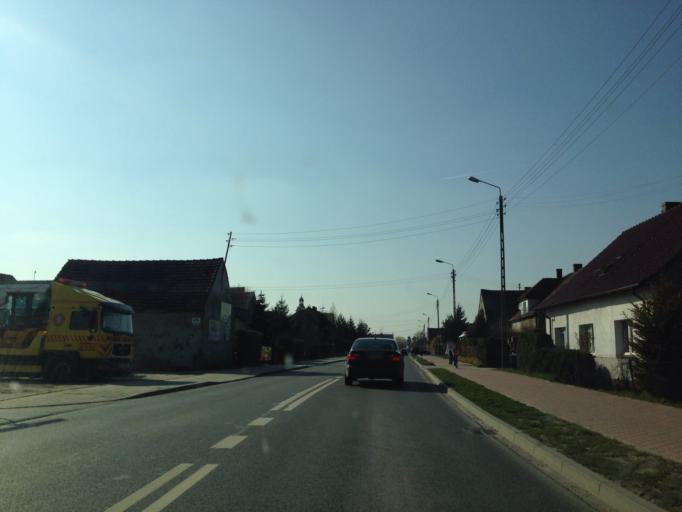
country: PL
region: Lower Silesian Voivodeship
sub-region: Powiat wroclawski
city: Kielczow
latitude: 51.1381
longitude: 17.1847
